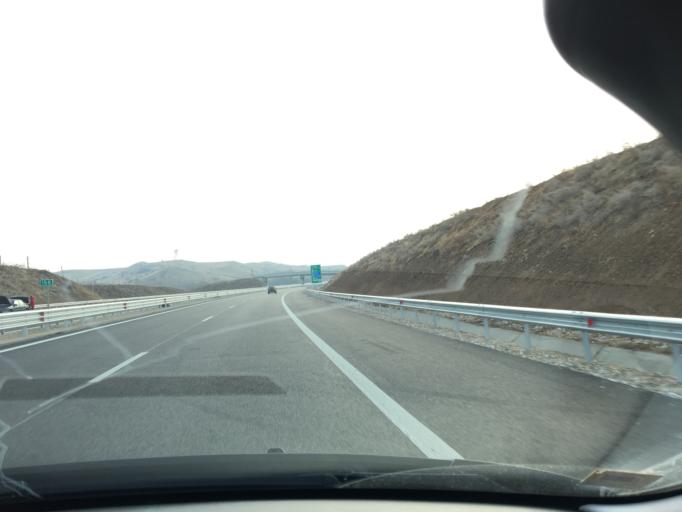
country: BG
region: Blagoevgrad
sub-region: Obshtina Sandanski
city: Sandanski
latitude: 41.5256
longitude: 23.2675
